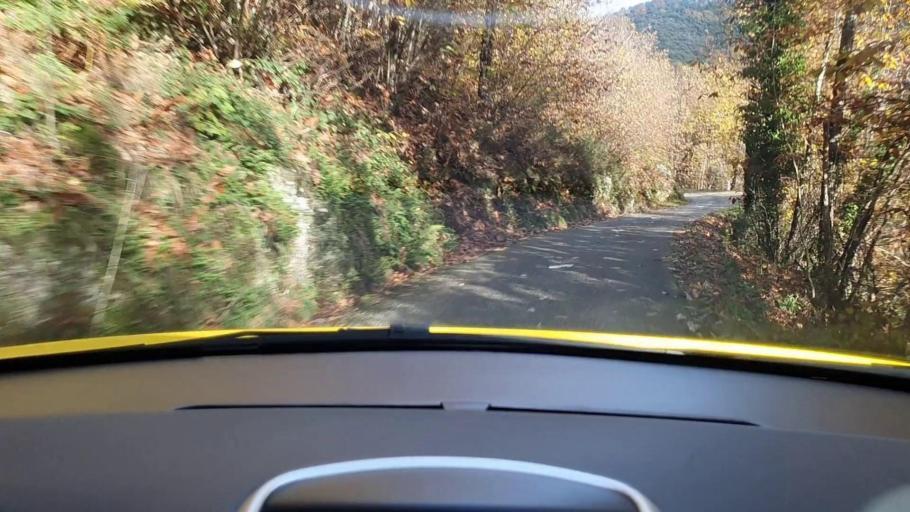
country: FR
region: Languedoc-Roussillon
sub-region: Departement du Gard
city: Valleraugue
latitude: 44.0966
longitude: 3.7417
